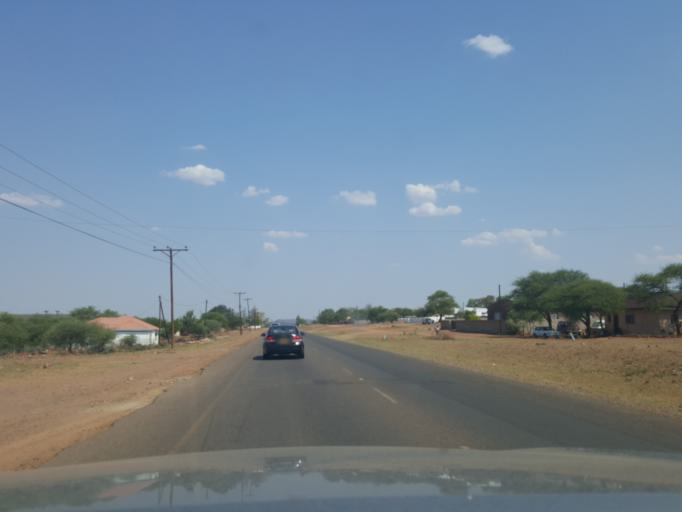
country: BW
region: South East
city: Ramotswa
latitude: -24.8416
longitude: 25.8239
